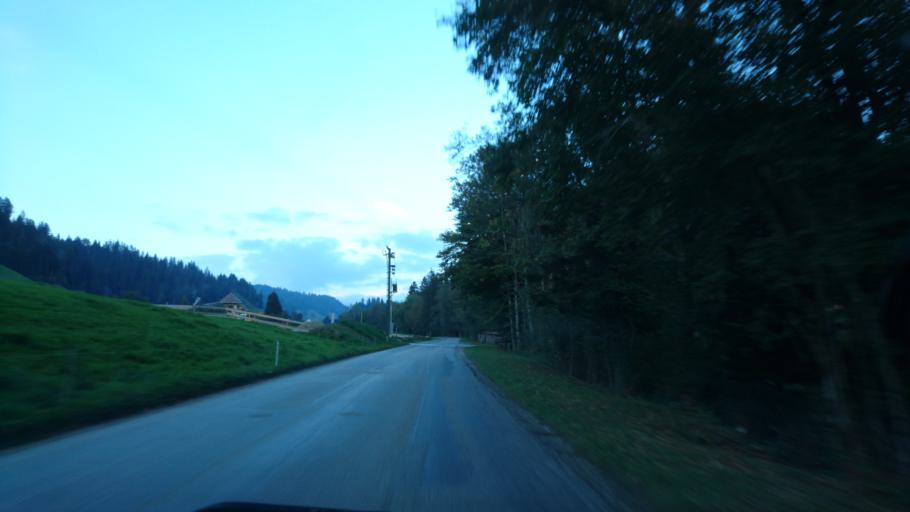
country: CH
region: Bern
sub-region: Emmental District
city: Trub
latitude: 46.9577
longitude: 7.8961
